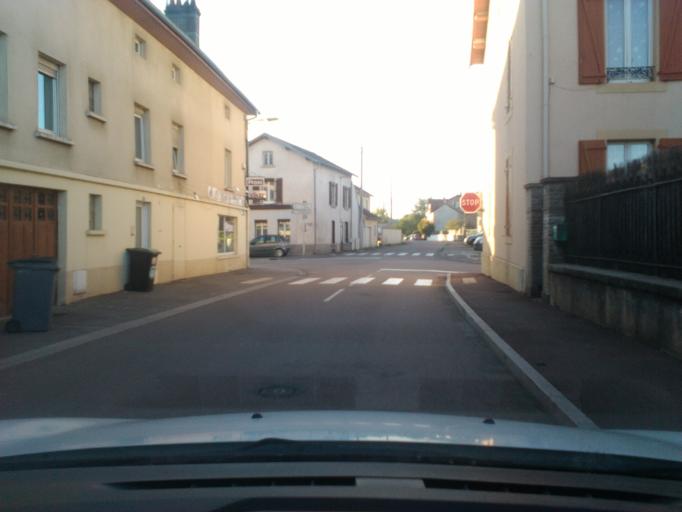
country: FR
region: Lorraine
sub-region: Departement des Vosges
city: Vincey
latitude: 48.3374
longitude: 6.3287
